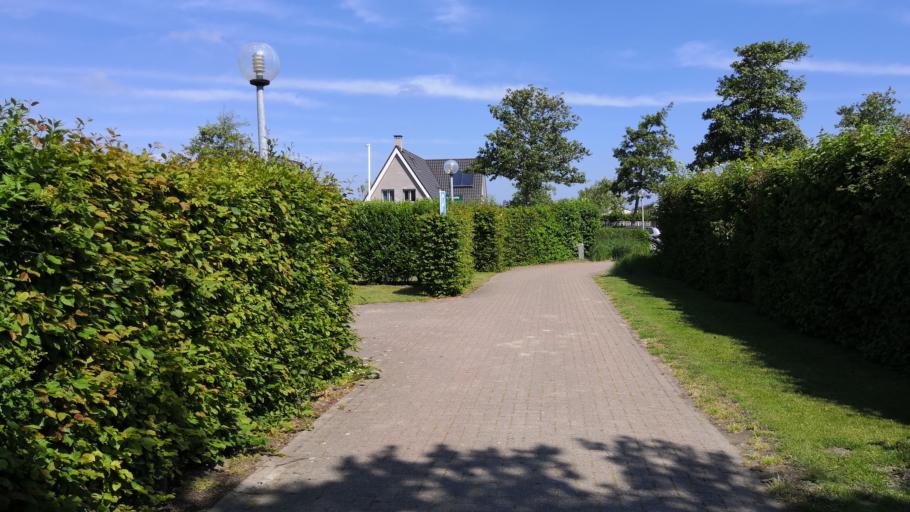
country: NL
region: Zeeland
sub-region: Gemeente Middelburg
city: Middelburg
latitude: 51.5546
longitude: 3.5157
